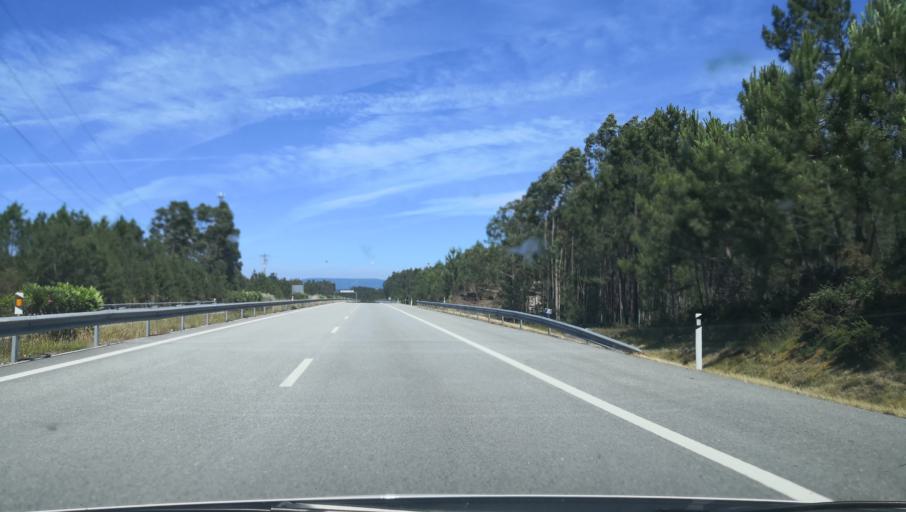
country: PT
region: Coimbra
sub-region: Montemor-O-Velho
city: Arazede
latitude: 40.2702
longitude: -8.6079
